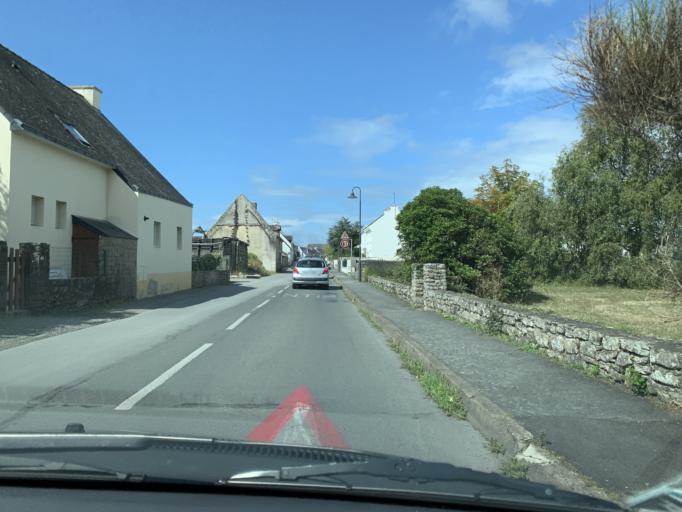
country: FR
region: Pays de la Loire
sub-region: Departement de la Loire-Atlantique
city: Le Pouliguen
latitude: 47.2955
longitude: -2.4263
